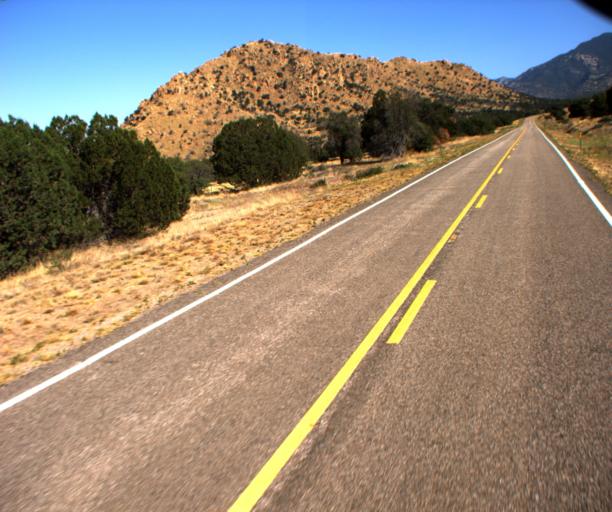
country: US
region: Arizona
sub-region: Graham County
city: Swift Trail Junction
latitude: 32.5796
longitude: -109.8503
